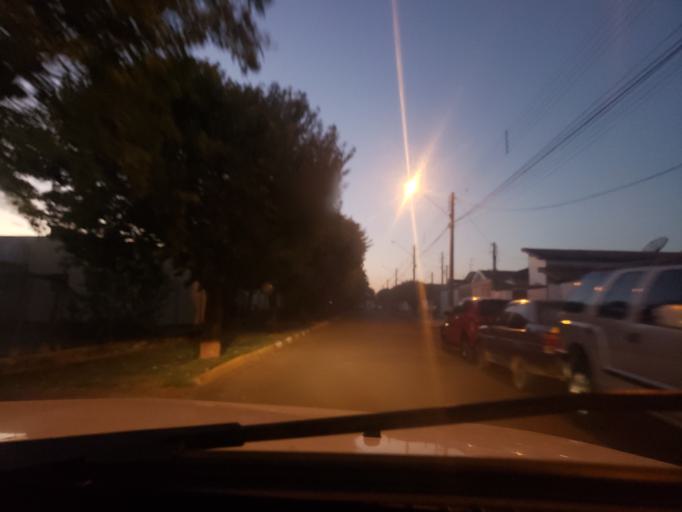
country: BR
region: Sao Paulo
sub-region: Conchal
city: Conchal
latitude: -22.2934
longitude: -47.1315
